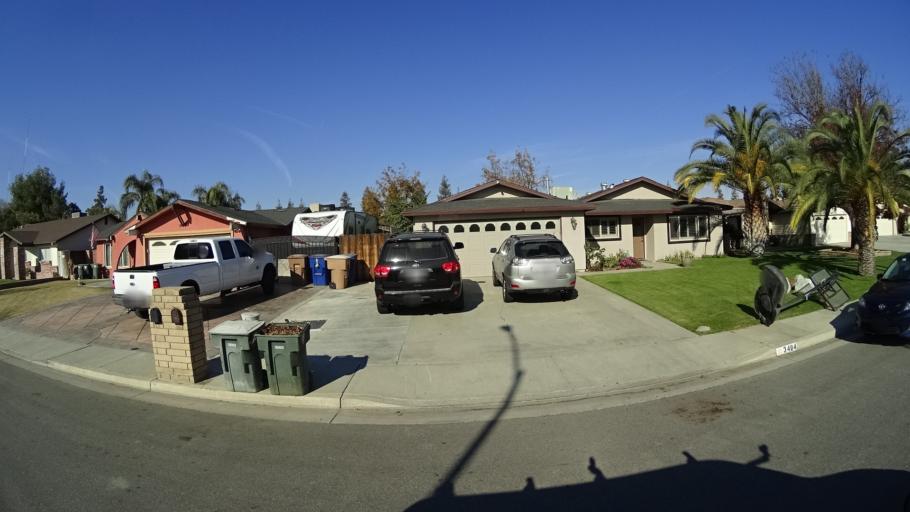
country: US
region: California
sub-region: Kern County
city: Greenfield
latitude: 35.3060
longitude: -119.0405
